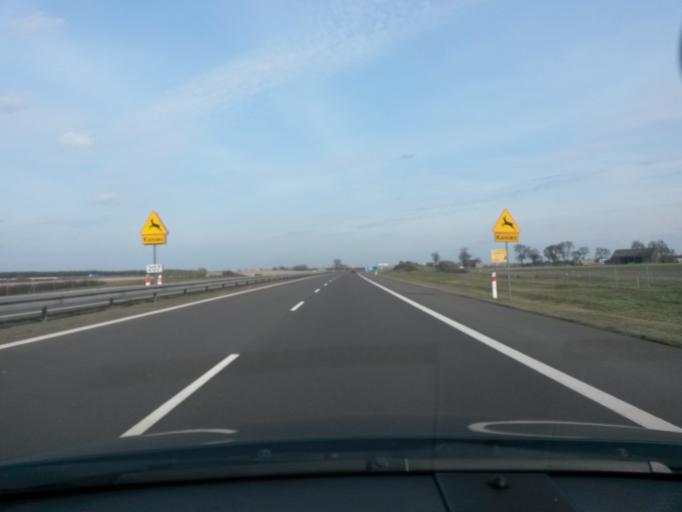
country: PL
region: Greater Poland Voivodeship
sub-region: Powiat wrzesinski
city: Wrzesnia
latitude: 52.3172
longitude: 17.5194
